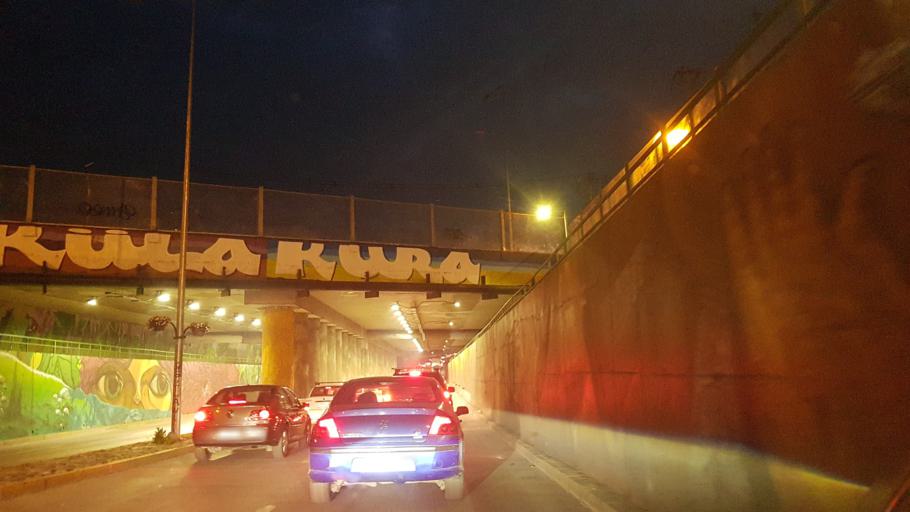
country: CL
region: Santiago Metropolitan
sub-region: Provincia de Santiago
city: Lo Prado
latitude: -33.3566
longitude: -70.7129
